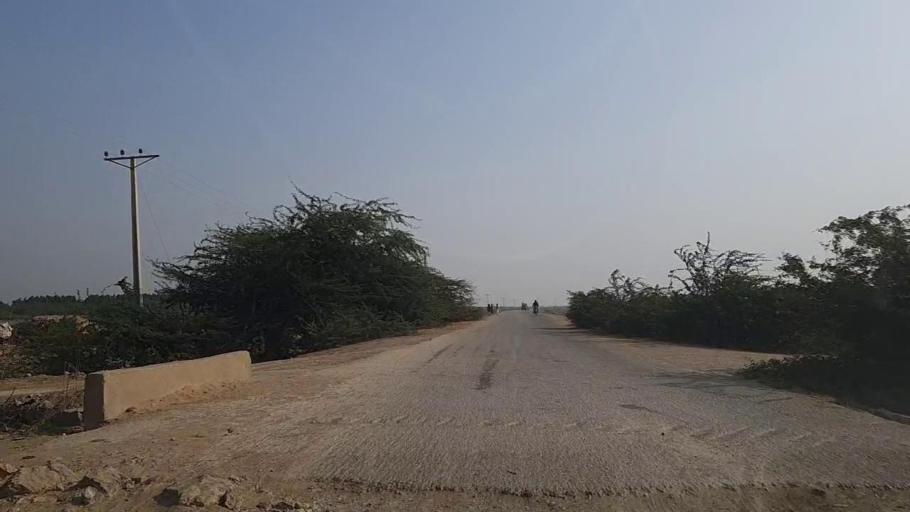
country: PK
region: Sindh
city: Keti Bandar
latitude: 24.2300
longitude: 67.6100
